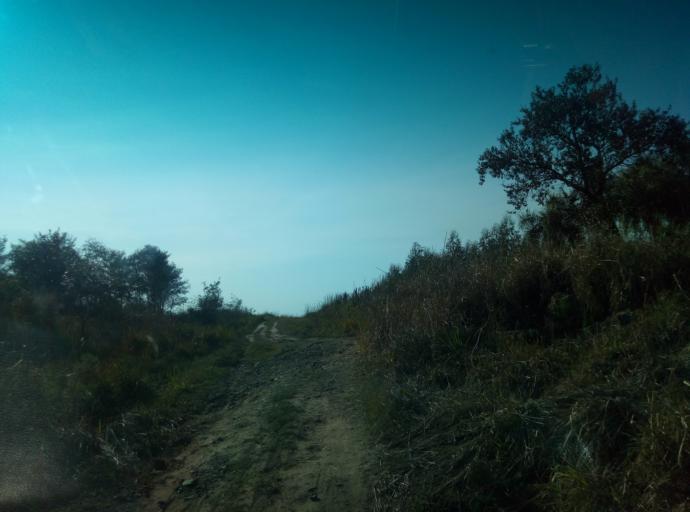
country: PY
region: Caaguazu
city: Doctor Cecilio Baez
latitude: -25.1911
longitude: -56.1980
